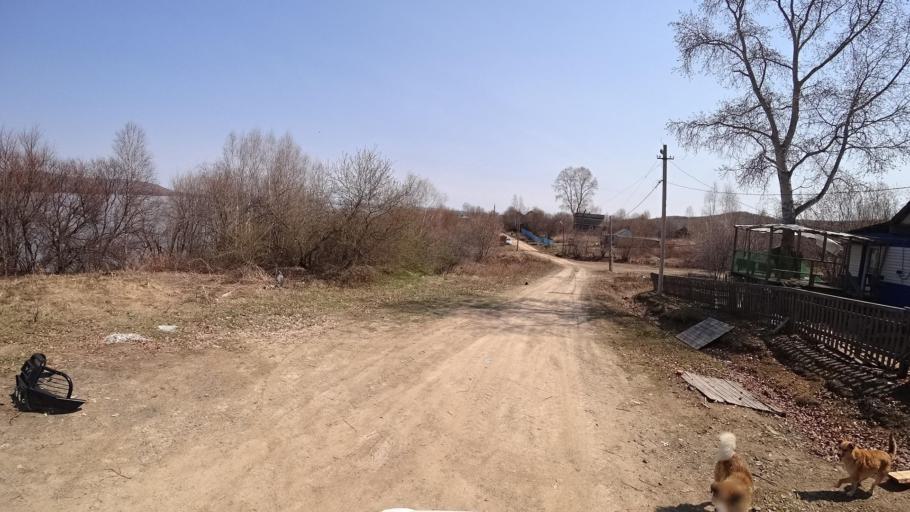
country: RU
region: Khabarovsk Krai
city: Selikhino
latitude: 50.6711
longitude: 137.3944
